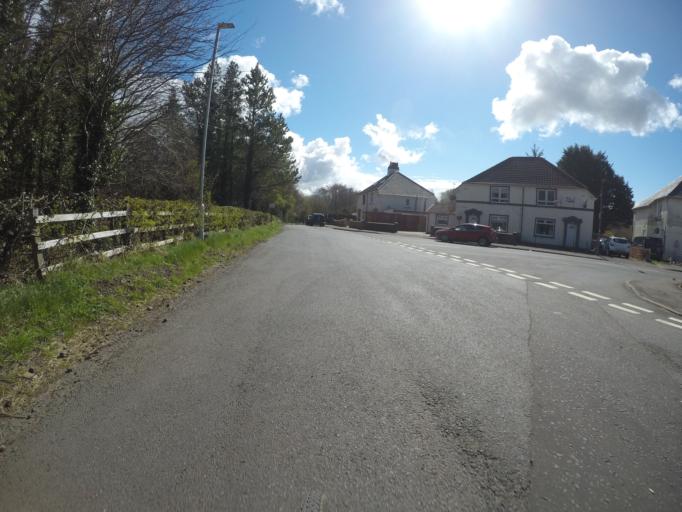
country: GB
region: Scotland
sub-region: North Ayrshire
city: Kilwinning
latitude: 55.6518
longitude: -4.6933
